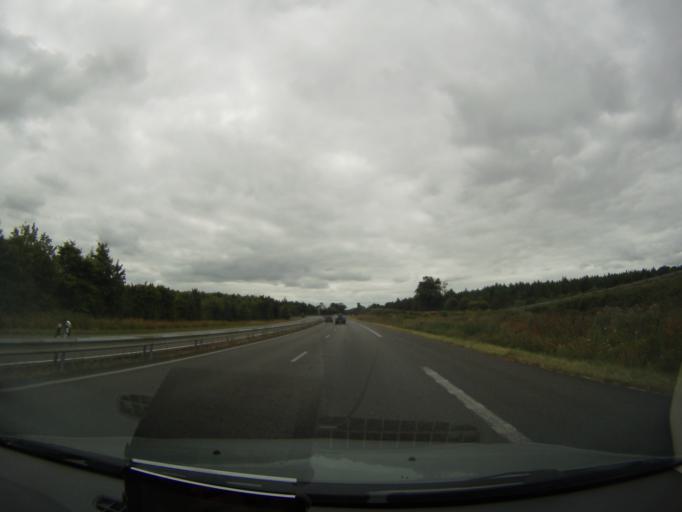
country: FR
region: Pays de la Loire
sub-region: Departement de la Loire-Atlantique
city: Heric
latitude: 47.4155
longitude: -1.6422
